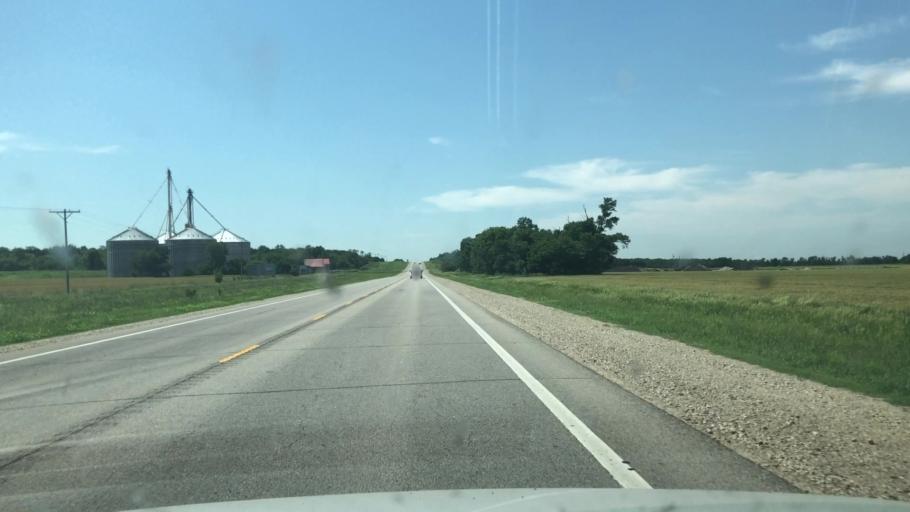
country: US
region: Kansas
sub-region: Butler County
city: Douglass
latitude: 37.3804
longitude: -97.0070
